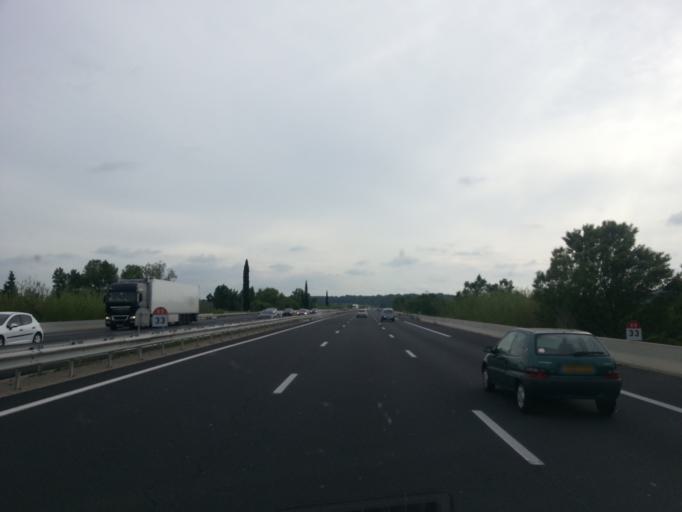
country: FR
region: Languedoc-Roussillon
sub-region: Departement du Gard
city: Sernhac
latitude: 43.9131
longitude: 4.5702
